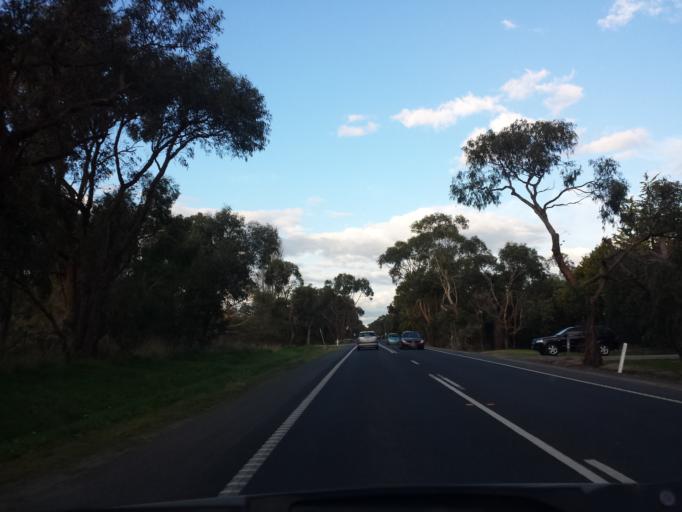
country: AU
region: Victoria
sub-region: Casey
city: Narre Warren North
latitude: -37.9656
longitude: 145.3252
